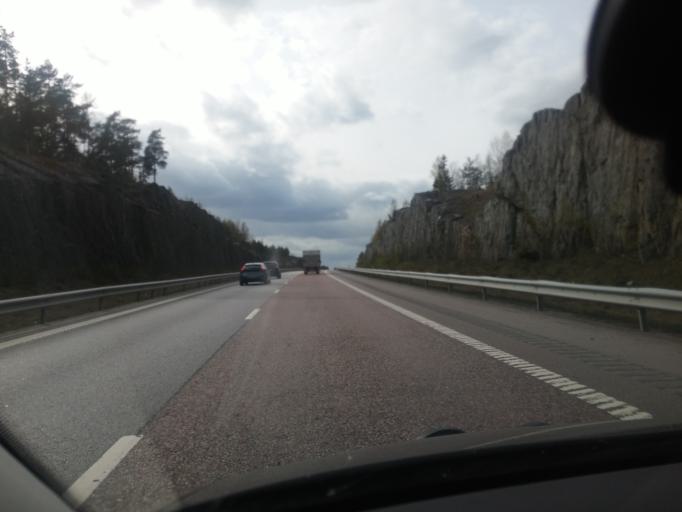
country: SE
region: Uppsala
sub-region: Enkopings Kommun
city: Dalby
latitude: 59.6259
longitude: 17.3753
